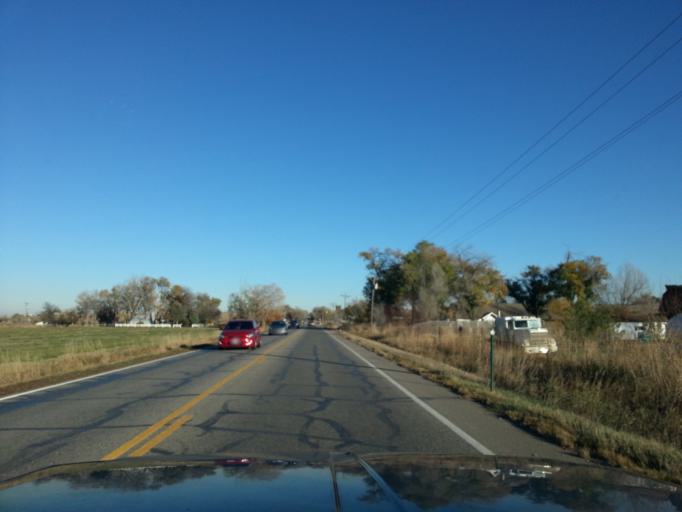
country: US
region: Colorado
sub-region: Larimer County
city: Loveland
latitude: 40.3783
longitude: -105.0388
